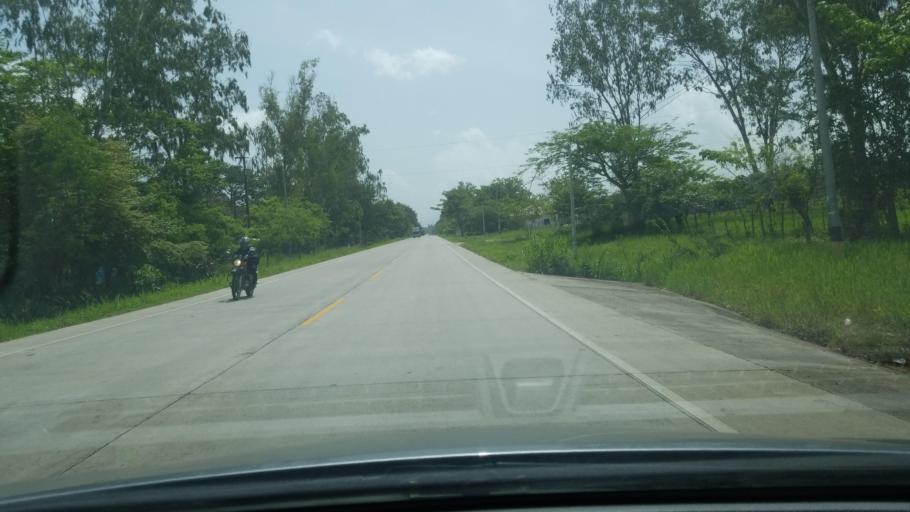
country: HN
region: Copan
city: Florida
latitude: 15.0419
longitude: -88.8153
